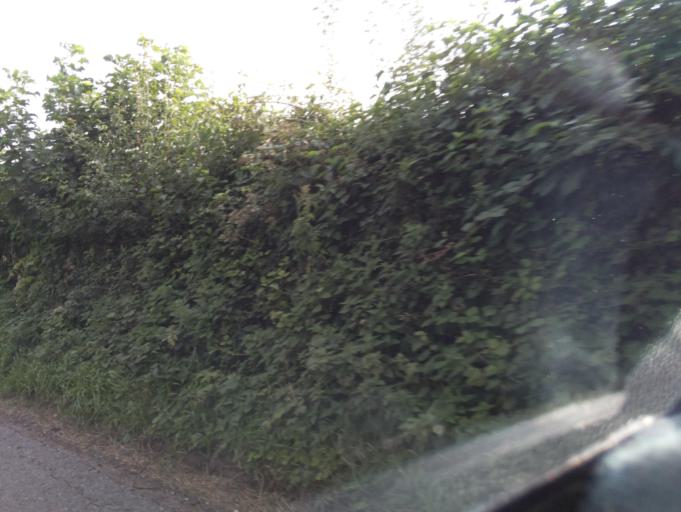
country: GB
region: England
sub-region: North Somerset
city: Winford
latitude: 51.3908
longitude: -2.6632
